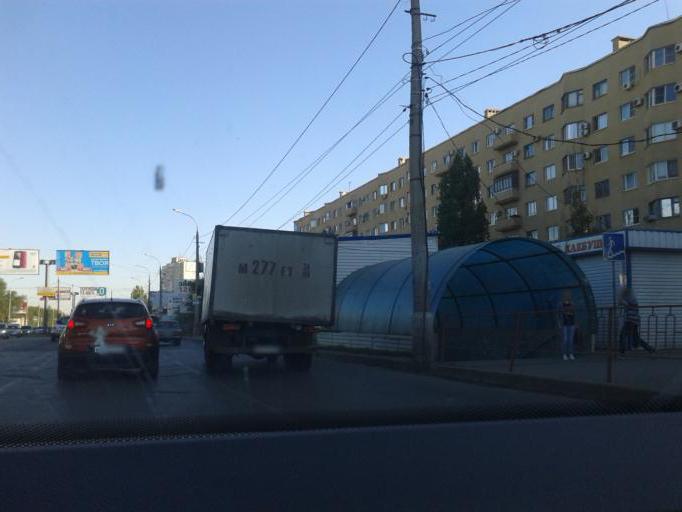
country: RU
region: Volgograd
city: Volgograd
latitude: 48.6743
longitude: 44.4437
